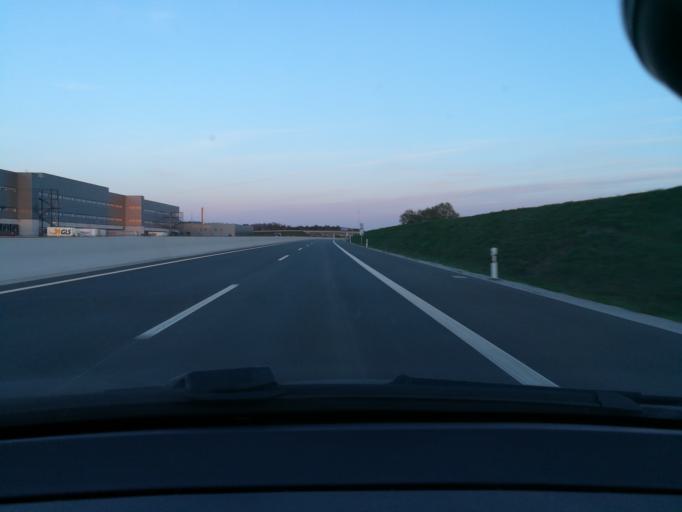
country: DE
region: North Rhine-Westphalia
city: Halle
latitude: 52.0260
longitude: 8.3720
